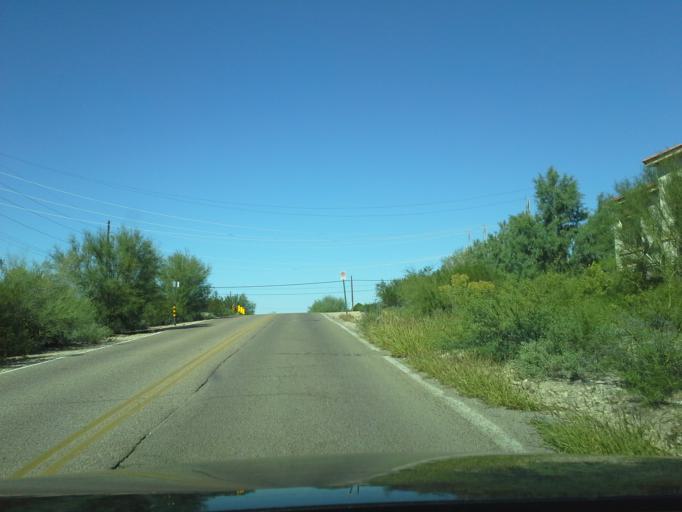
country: US
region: Arizona
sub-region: Pima County
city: South Tucson
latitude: 32.2220
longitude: -111.0288
